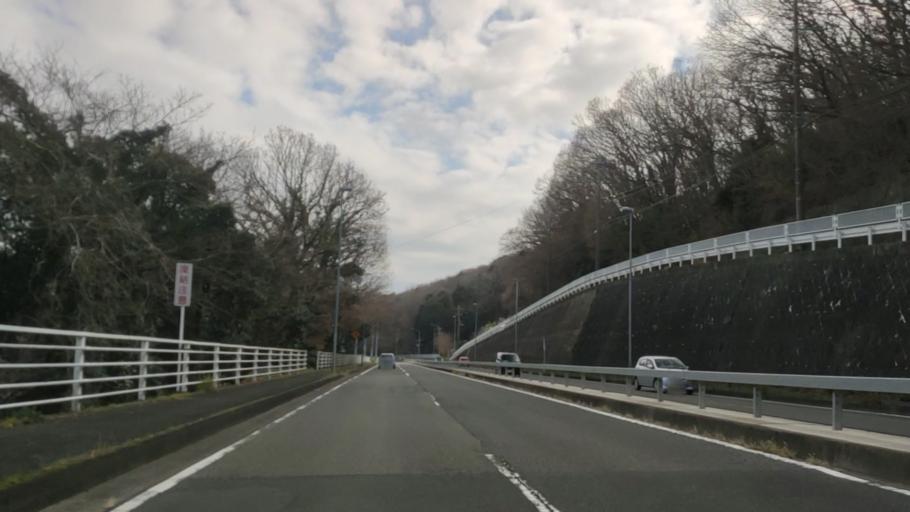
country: JP
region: Kanagawa
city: Ninomiya
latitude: 35.3304
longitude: 139.2322
